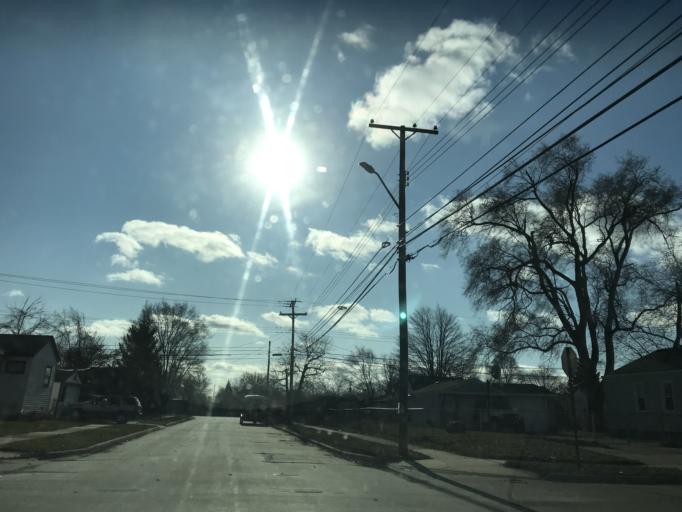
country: US
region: Michigan
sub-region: Oakland County
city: Madison Heights
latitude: 42.4786
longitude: -83.1016
